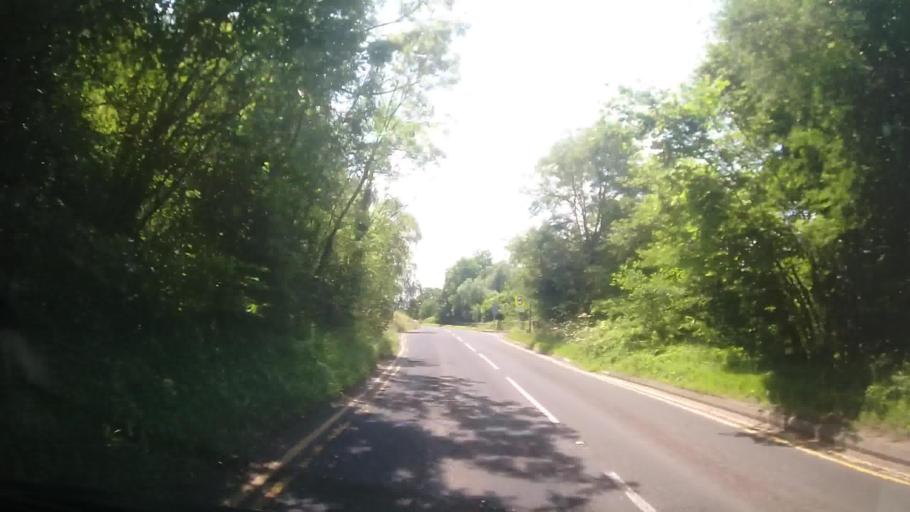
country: GB
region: England
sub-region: Herefordshire
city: Brockhampton
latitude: 52.0257
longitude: -2.6291
